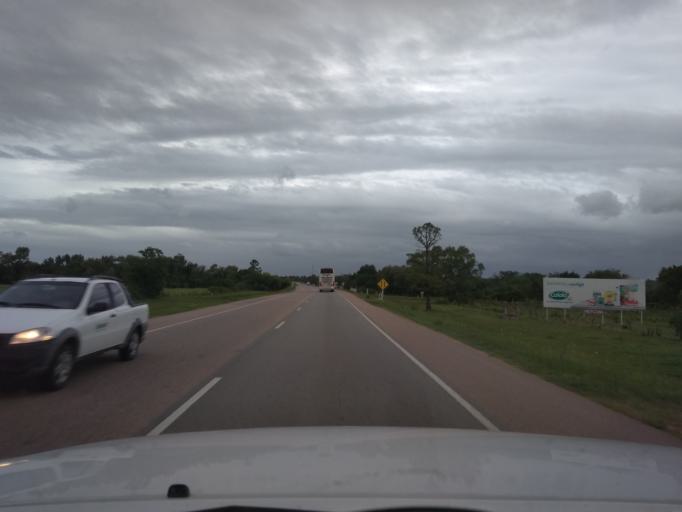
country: UY
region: Canelones
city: Canelones
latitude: -34.4961
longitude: -56.2820
